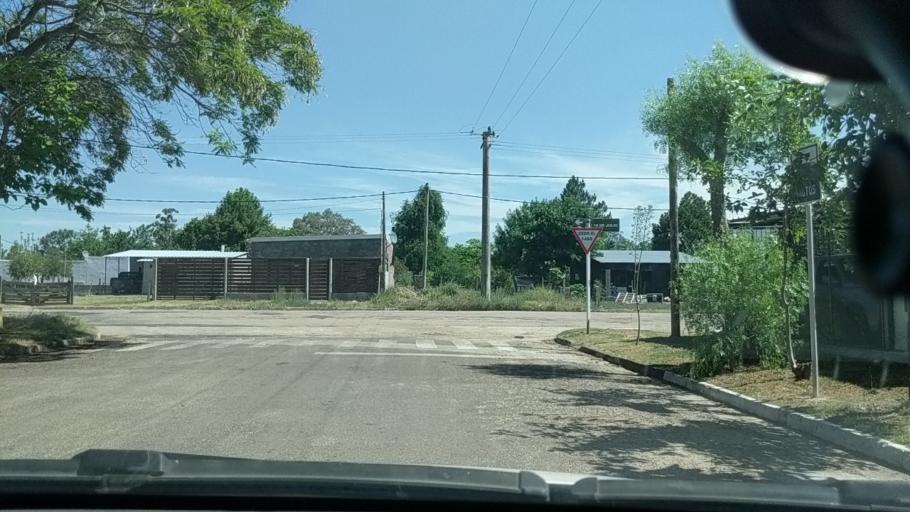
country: UY
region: Tacuarembo
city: Paso de los Toros
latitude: -32.8099
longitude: -56.5305
